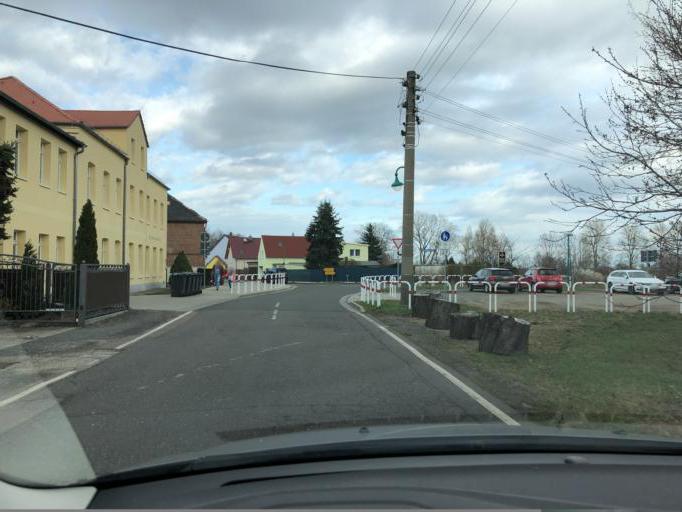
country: DE
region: Saxony
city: Markranstadt
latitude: 51.2788
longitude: 12.2291
